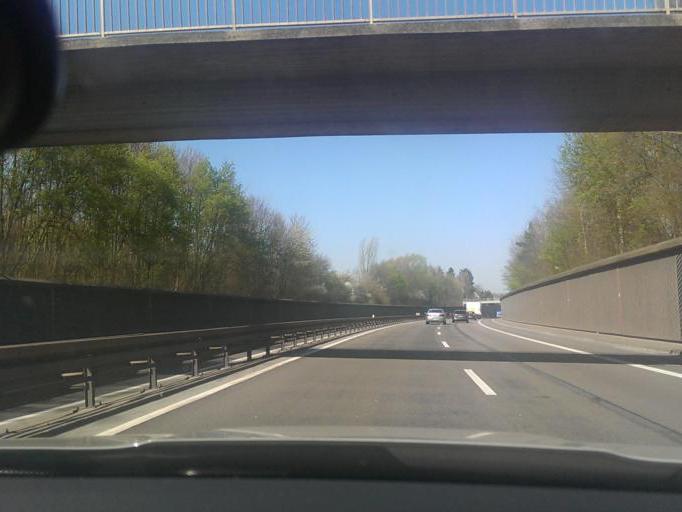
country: DE
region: Lower Saxony
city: Langenhagen
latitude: 52.4326
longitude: 9.7255
